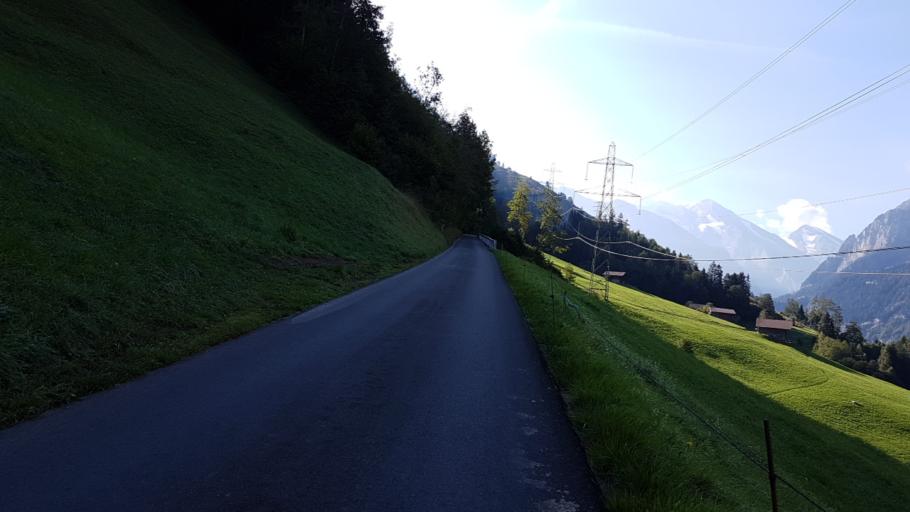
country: CH
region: Bern
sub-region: Frutigen-Niedersimmental District
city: Frutigen
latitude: 46.5593
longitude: 7.6691
